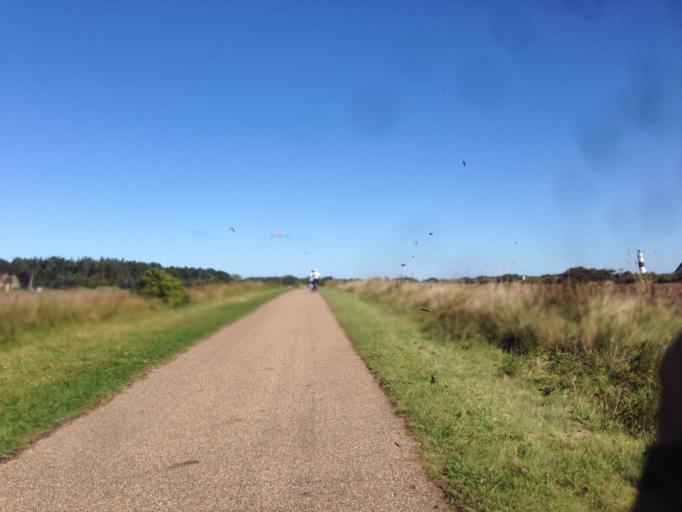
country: DE
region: Schleswig-Holstein
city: Tinnum
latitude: 54.9405
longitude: 8.3315
